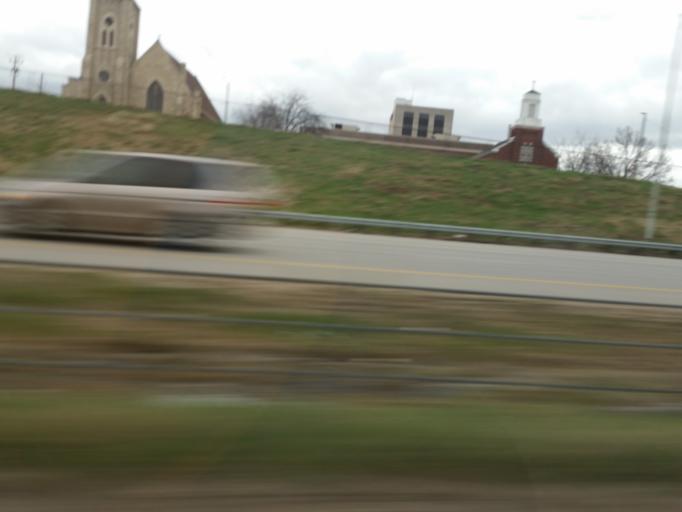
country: US
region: Iowa
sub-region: Linn County
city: Cedar Rapids
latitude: 41.9823
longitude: -91.6665
